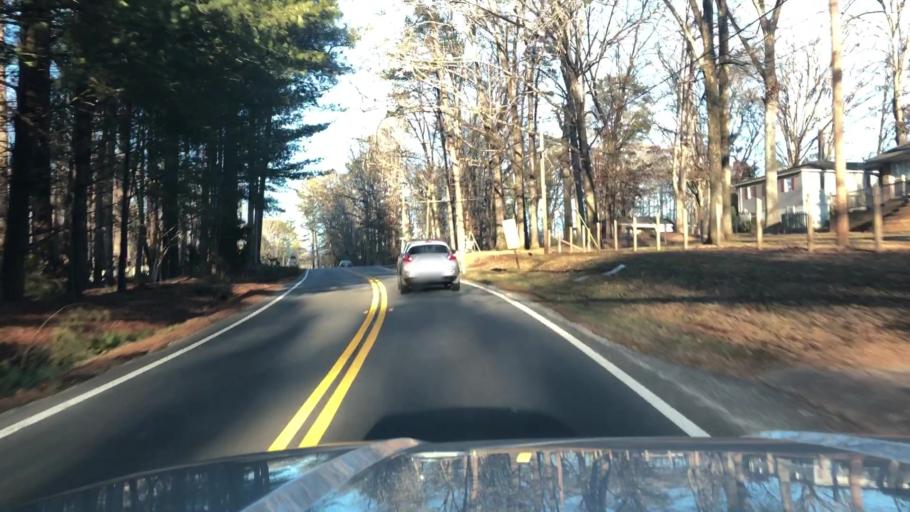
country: US
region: Georgia
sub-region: Cherokee County
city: Canton
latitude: 34.2109
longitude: -84.5127
